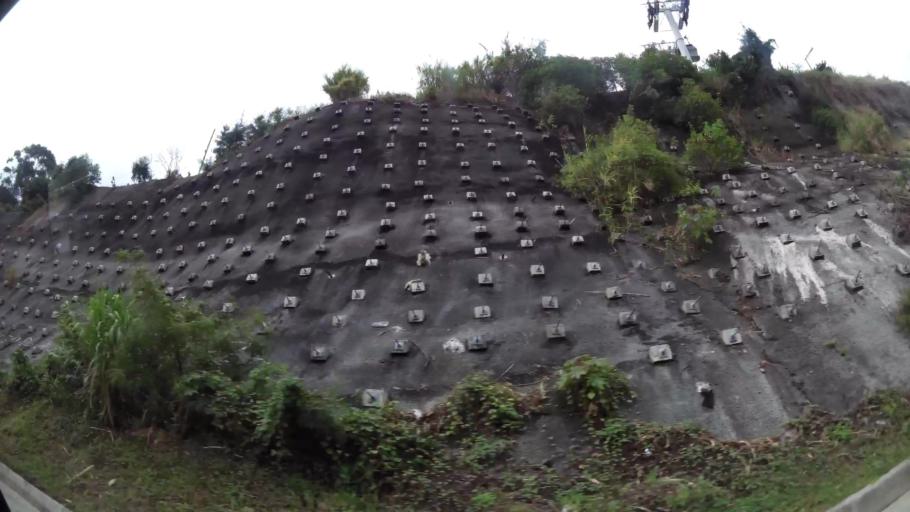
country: CO
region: Antioquia
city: Medellin
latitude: 6.2738
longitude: -75.6138
